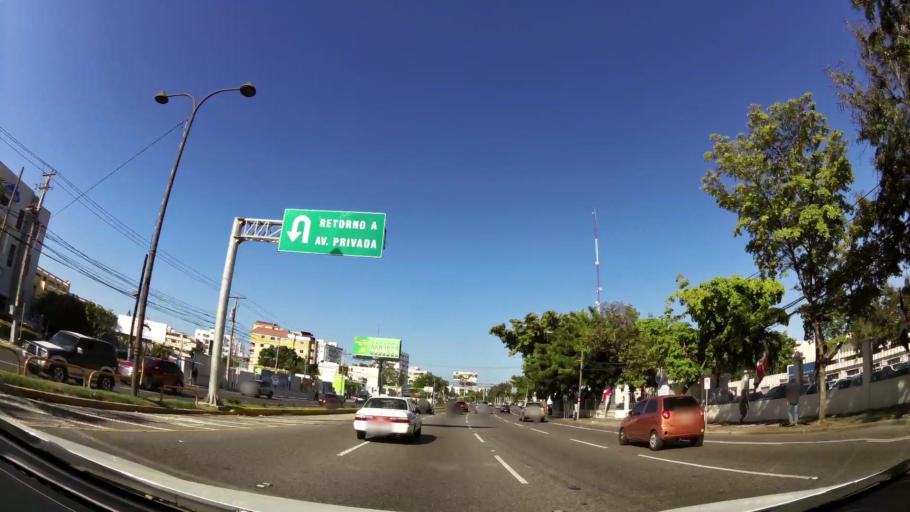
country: DO
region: Nacional
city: Bella Vista
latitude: 18.4500
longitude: -69.9677
